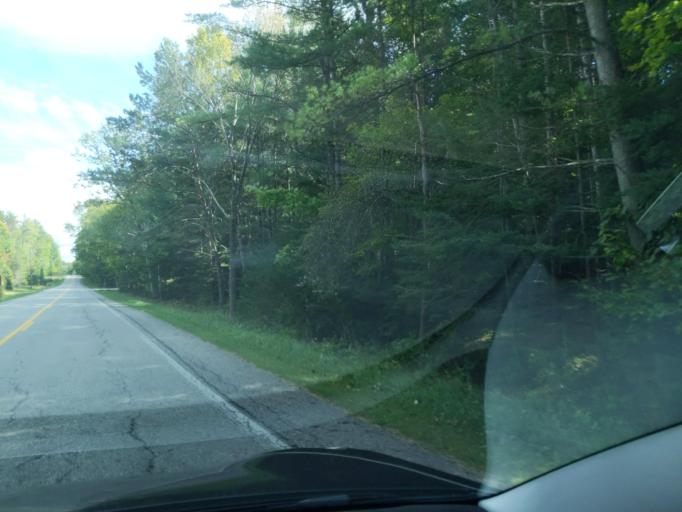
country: US
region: Michigan
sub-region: Antrim County
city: Bellaire
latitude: 45.0498
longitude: -85.3136
